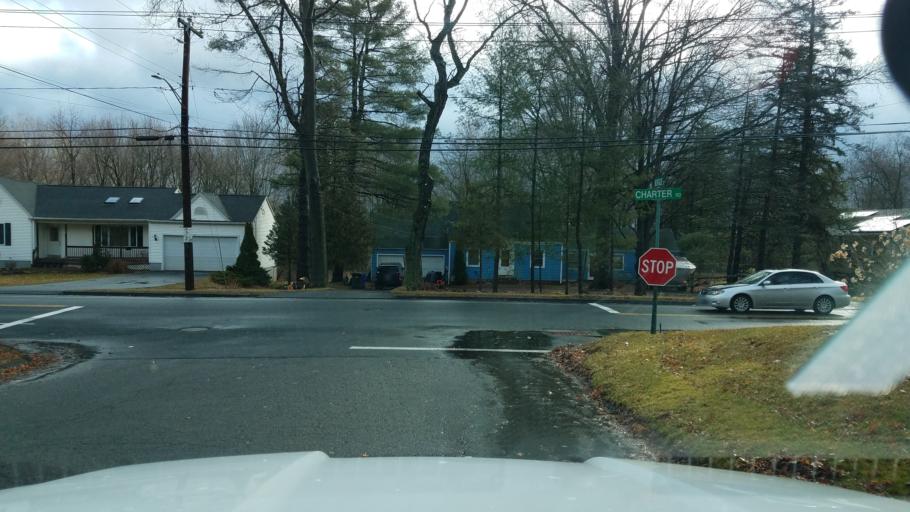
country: US
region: Connecticut
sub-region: Hartford County
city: Wethersfield
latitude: 41.6861
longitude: -72.6592
